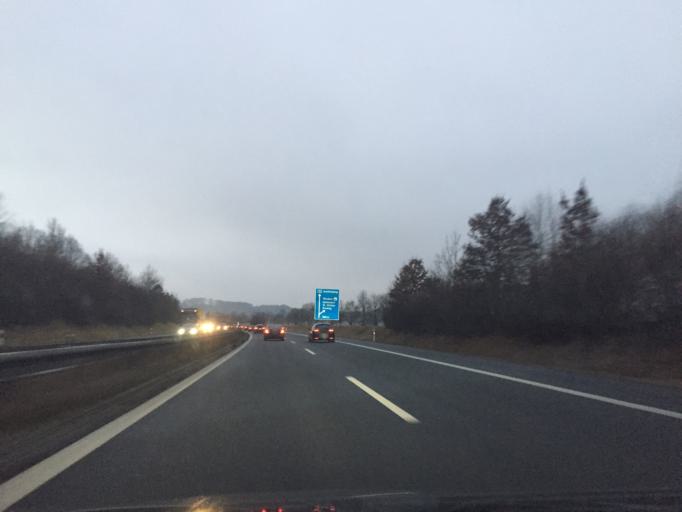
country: DE
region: Bavaria
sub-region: Upper Bavaria
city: Windach
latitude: 48.0741
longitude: 11.0490
